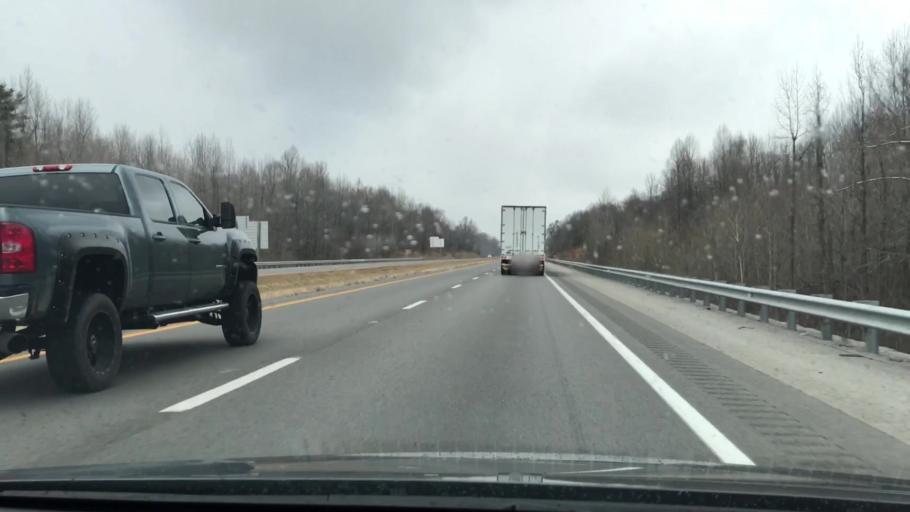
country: US
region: Kentucky
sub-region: Hopkins County
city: Earlington
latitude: 37.2687
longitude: -87.4538
